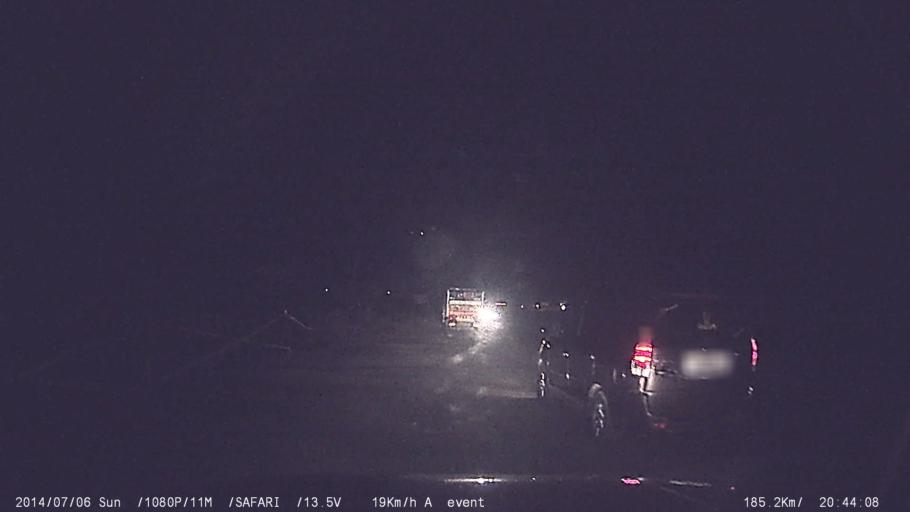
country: IN
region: Tamil Nadu
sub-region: Coimbatore
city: Madukkarai
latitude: 10.8532
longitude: 76.8437
